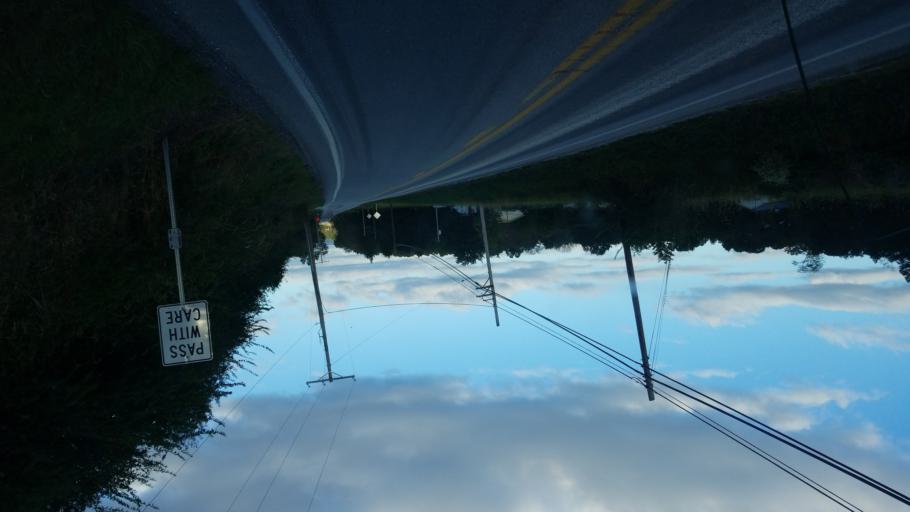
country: US
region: Pennsylvania
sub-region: Adams County
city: Lake Heritage
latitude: 39.8835
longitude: -77.1665
